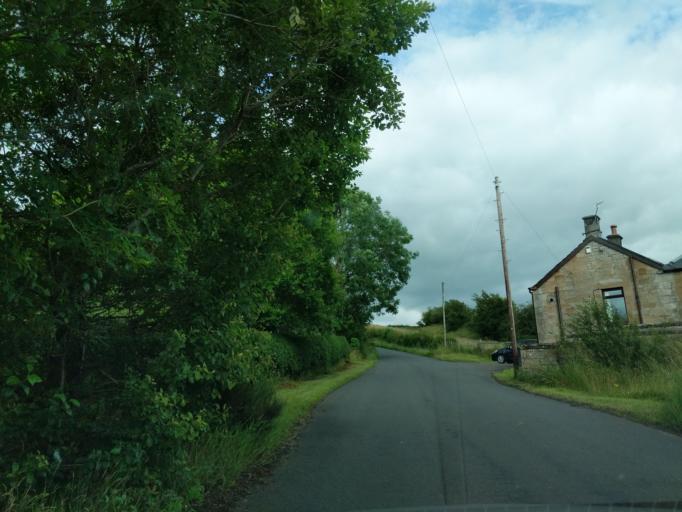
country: GB
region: Scotland
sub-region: South Lanarkshire
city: Larkhall
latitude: 55.7008
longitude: -3.9670
